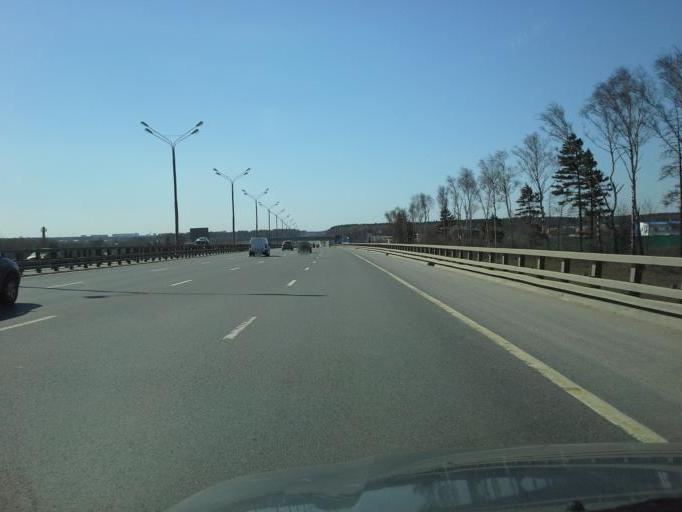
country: RU
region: Moskovskaya
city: Kokoshkino
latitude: 55.6228
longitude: 37.1425
